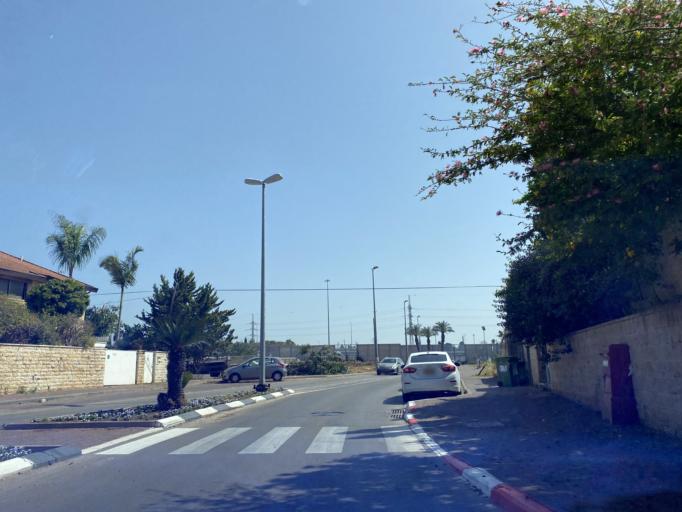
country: IL
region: Central District
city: Ra'anana
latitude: 32.1743
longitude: 34.8797
